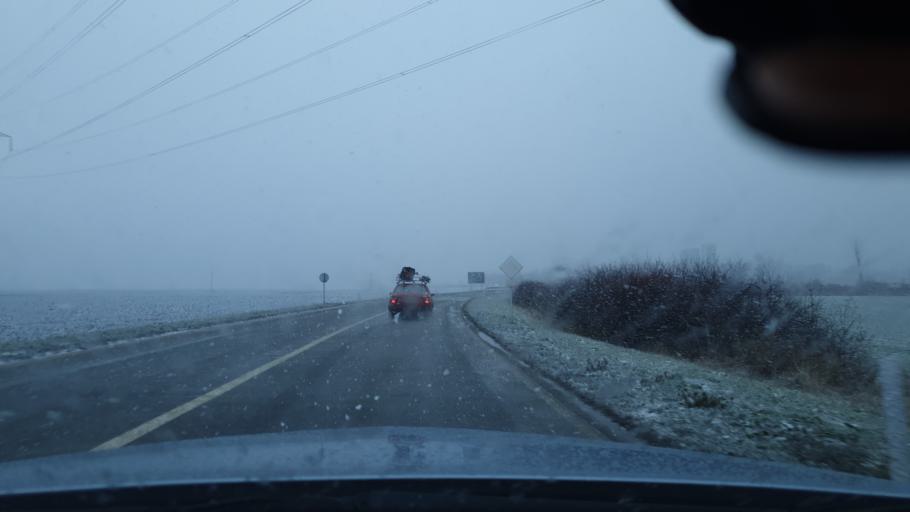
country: RS
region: Autonomna Pokrajina Vojvodina
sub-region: Juznobanatski Okrug
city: Pancevo
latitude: 44.8639
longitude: 20.7381
